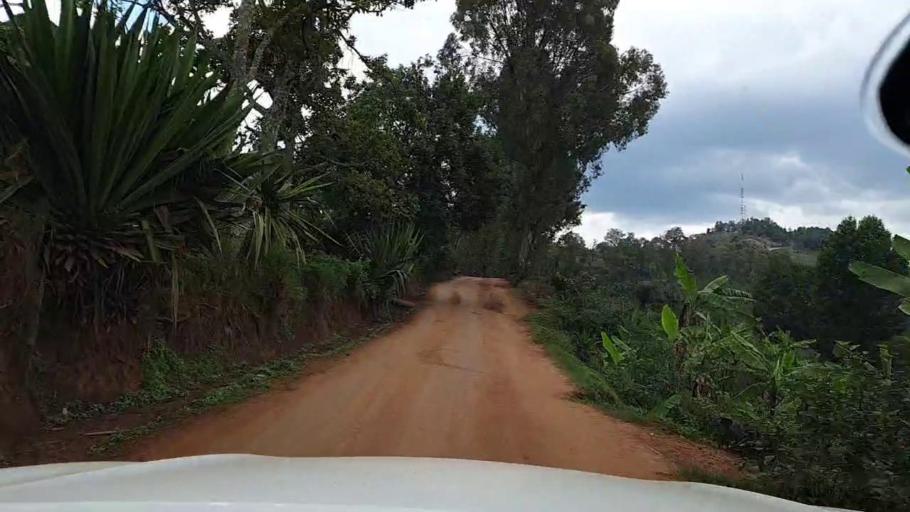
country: RW
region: Southern Province
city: Nzega
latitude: -2.7108
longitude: 29.5280
